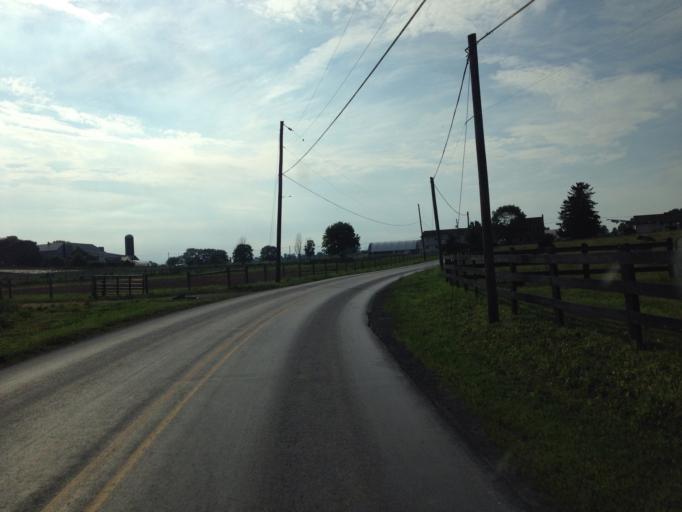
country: US
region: Pennsylvania
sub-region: Lancaster County
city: Strasburg
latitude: 40.0543
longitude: -76.1944
